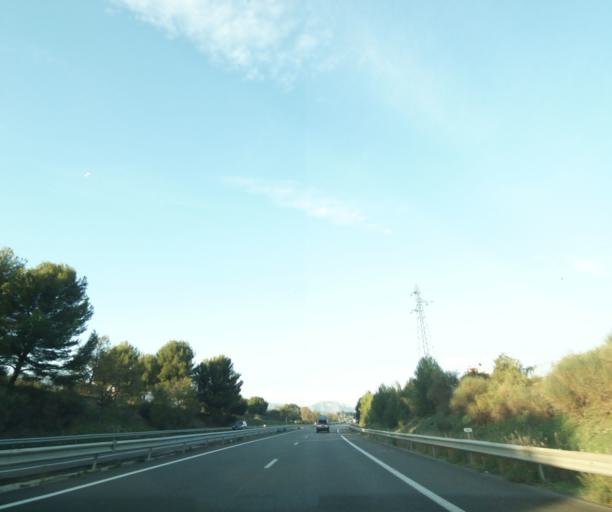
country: FR
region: Provence-Alpes-Cote d'Azur
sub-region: Departement des Bouches-du-Rhone
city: Aubagne
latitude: 43.2896
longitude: 5.5868
